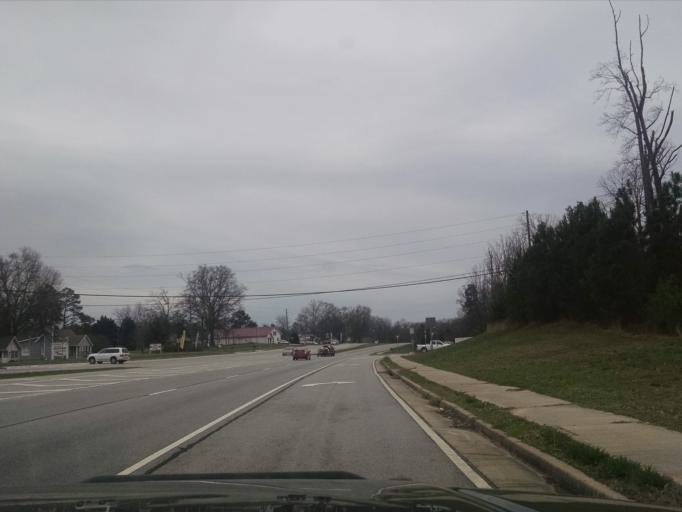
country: US
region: Georgia
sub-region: Hall County
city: Oakwood
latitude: 34.2076
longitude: -83.8567
